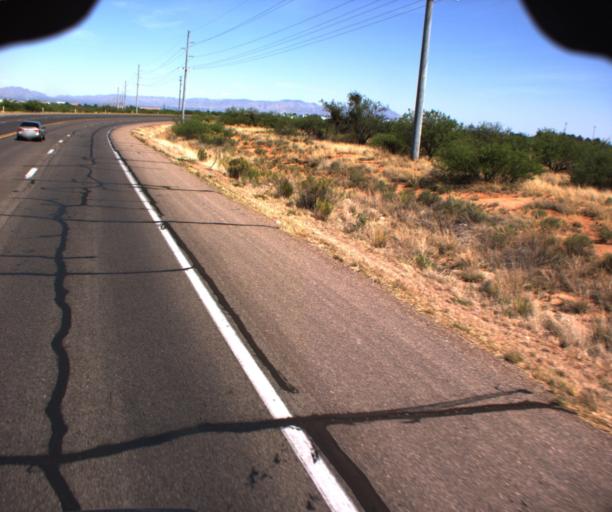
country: US
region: Arizona
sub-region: Cochise County
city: Sierra Vista
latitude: 31.5694
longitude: -110.2626
